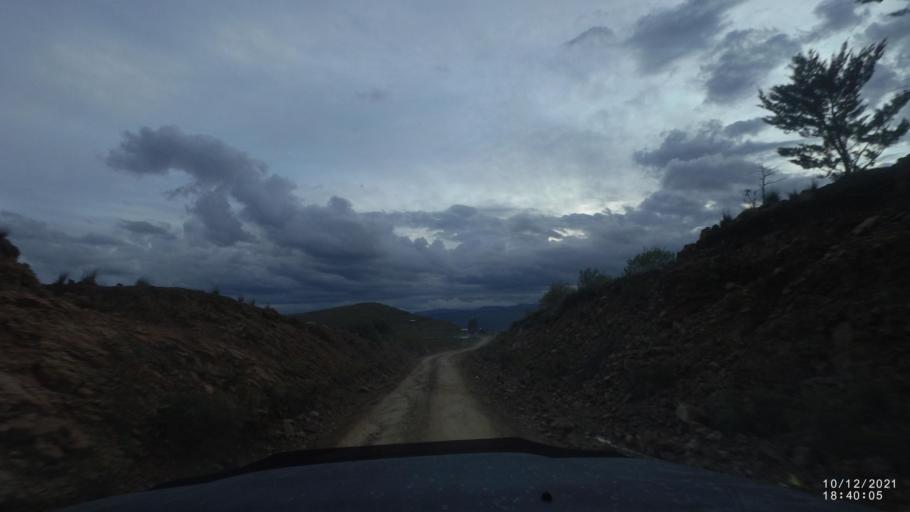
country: BO
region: Cochabamba
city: Tarata
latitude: -17.8550
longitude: -65.9886
